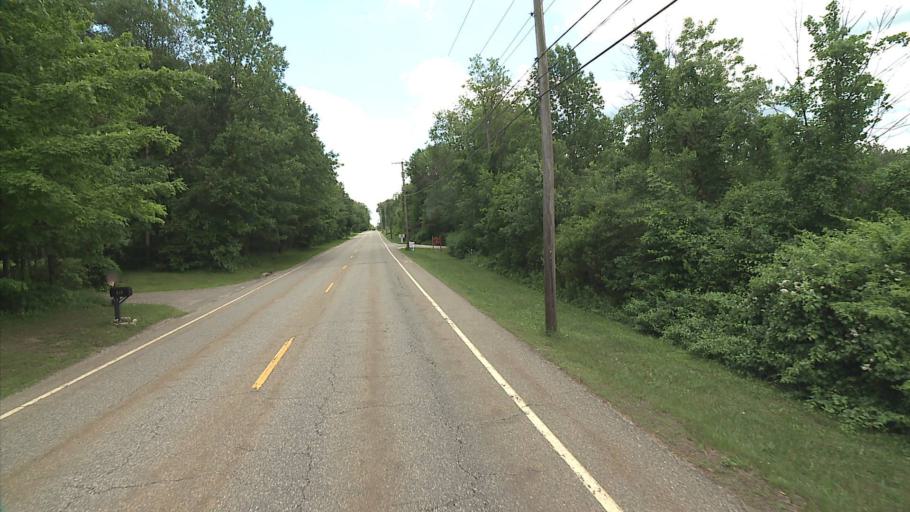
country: US
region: Connecticut
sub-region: Litchfield County
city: Litchfield
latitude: 41.8050
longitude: -73.2151
